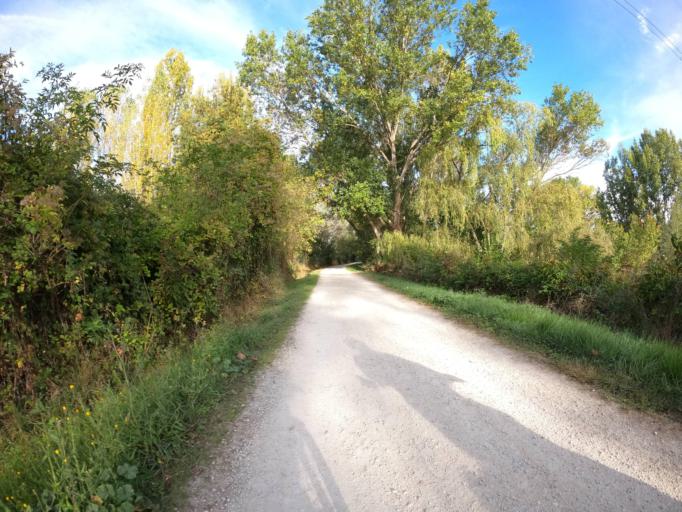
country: ES
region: Navarre
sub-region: Provincia de Navarra
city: Orkoien
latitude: 42.8105
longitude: -1.7188
